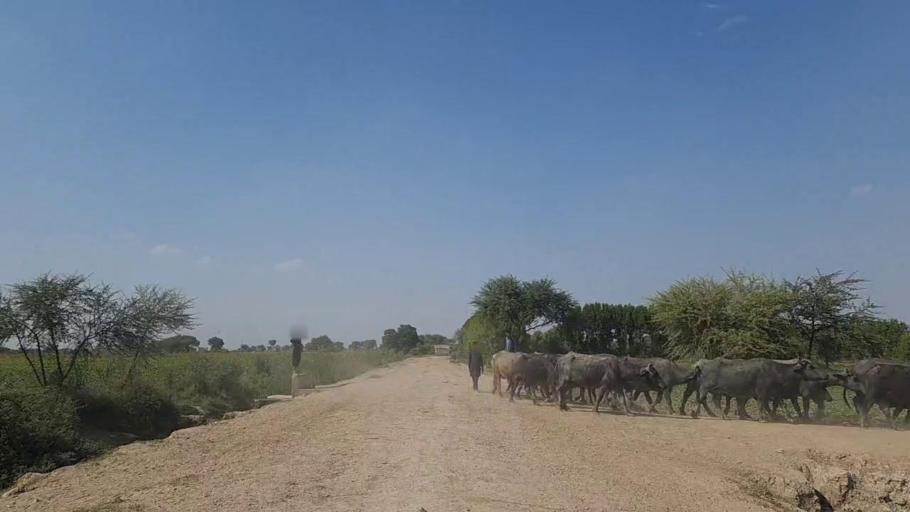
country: PK
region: Sindh
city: Jati
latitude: 24.5187
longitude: 68.2938
